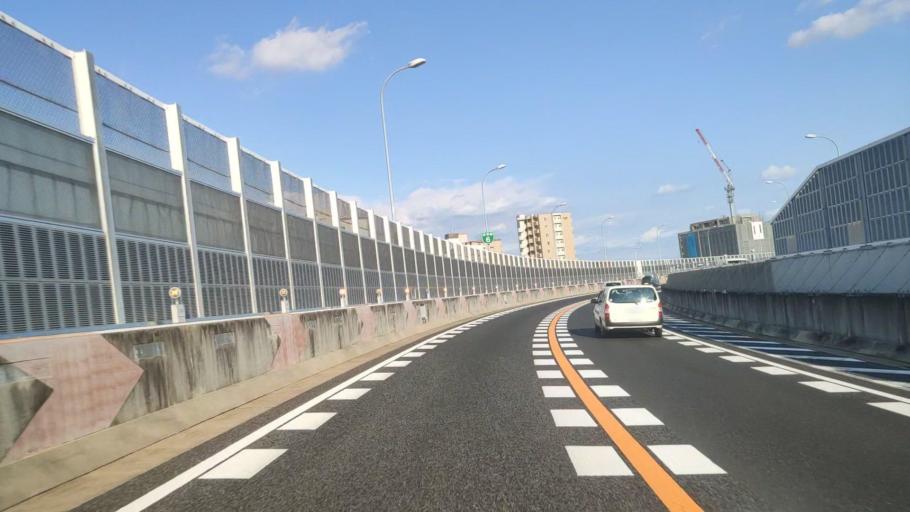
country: JP
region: Aichi
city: Nagoya-shi
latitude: 35.2028
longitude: 136.8901
